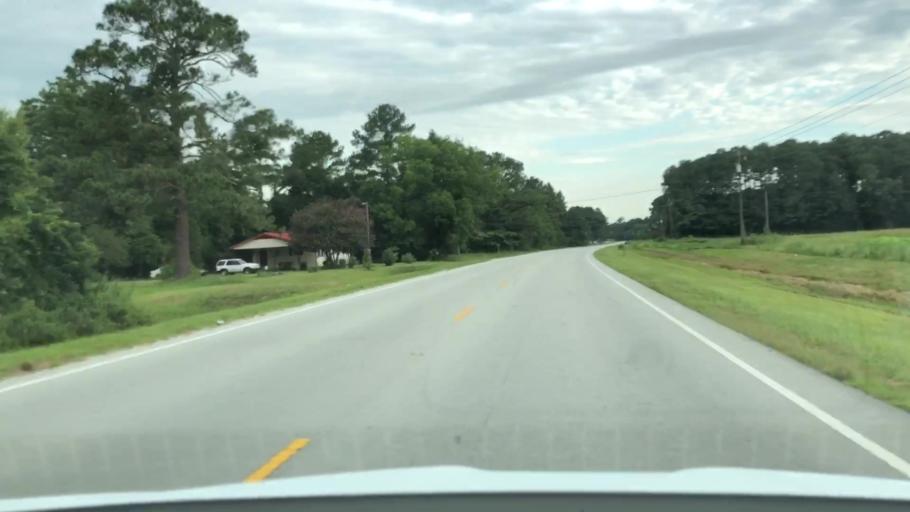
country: US
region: North Carolina
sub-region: Jones County
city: Trenton
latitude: 35.0209
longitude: -77.3039
